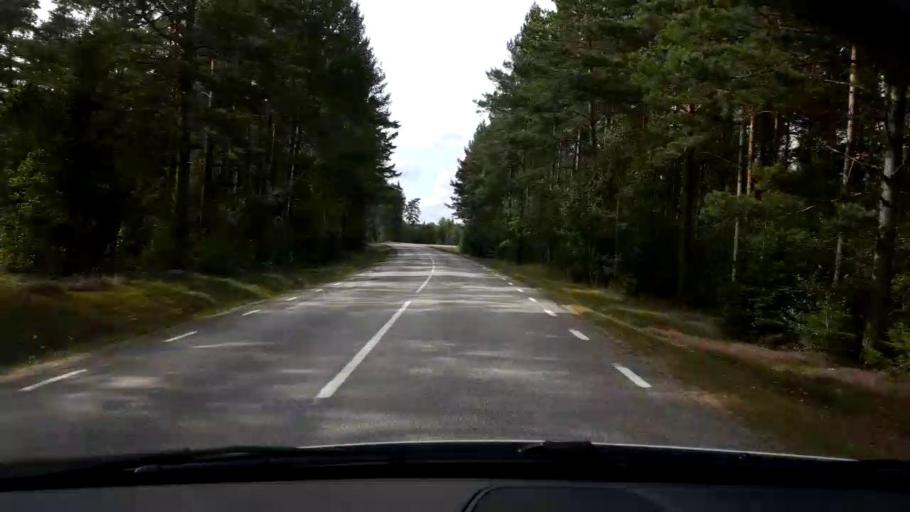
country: SE
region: Joenkoeping
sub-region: Vetlanda Kommun
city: Vetlanda
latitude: 57.3621
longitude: 15.0671
